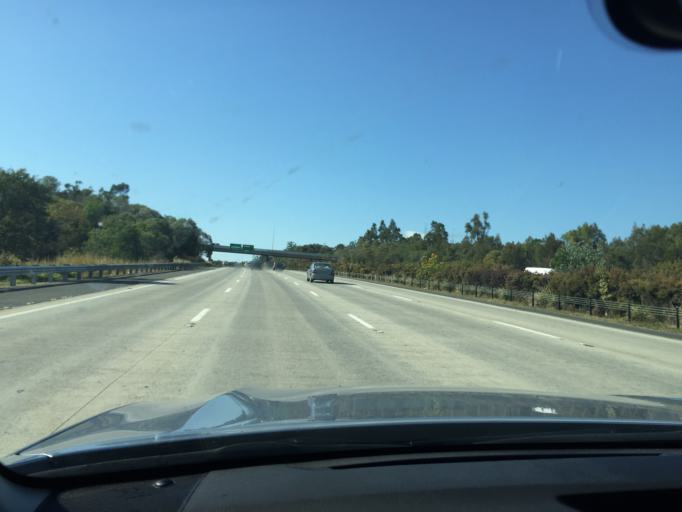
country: AU
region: Queensland
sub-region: Gold Coast
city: Ormeau Hills
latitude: -27.8037
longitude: 153.2641
